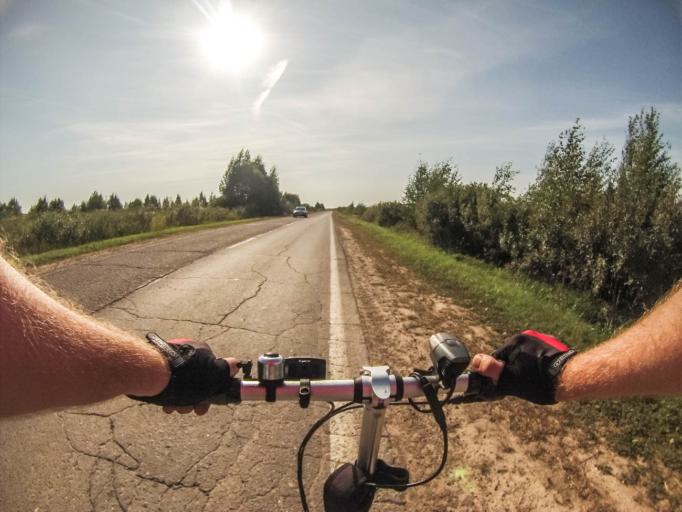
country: RU
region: Jaroslavl
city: Myshkin
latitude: 57.7735
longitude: 38.3236
